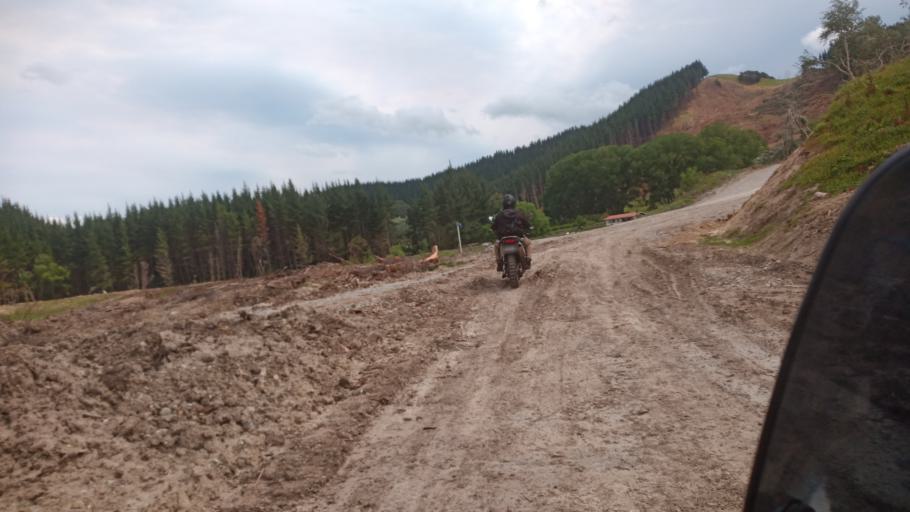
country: NZ
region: Gisborne
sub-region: Gisborne District
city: Gisborne
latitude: -38.4629
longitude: 177.9054
